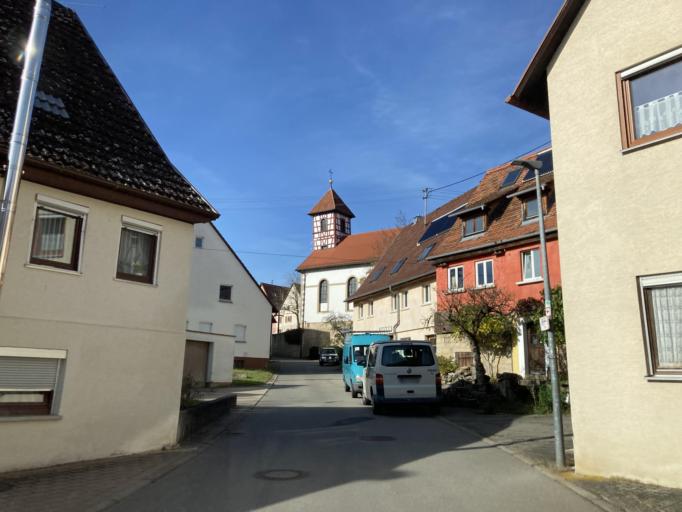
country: DE
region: Baden-Wuerttemberg
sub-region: Tuebingen Region
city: Rottenburg
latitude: 48.4497
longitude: 8.9269
